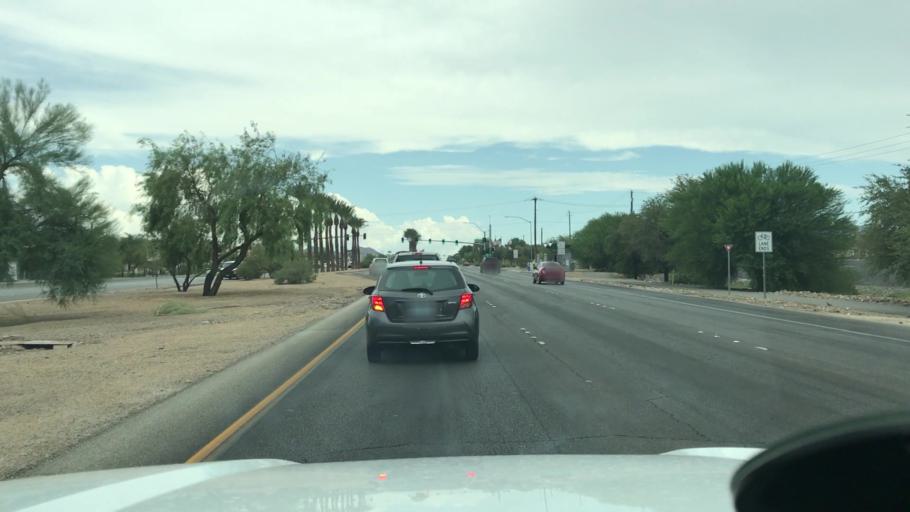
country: US
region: Nevada
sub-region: Clark County
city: Henderson
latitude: 36.0409
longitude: -114.9837
